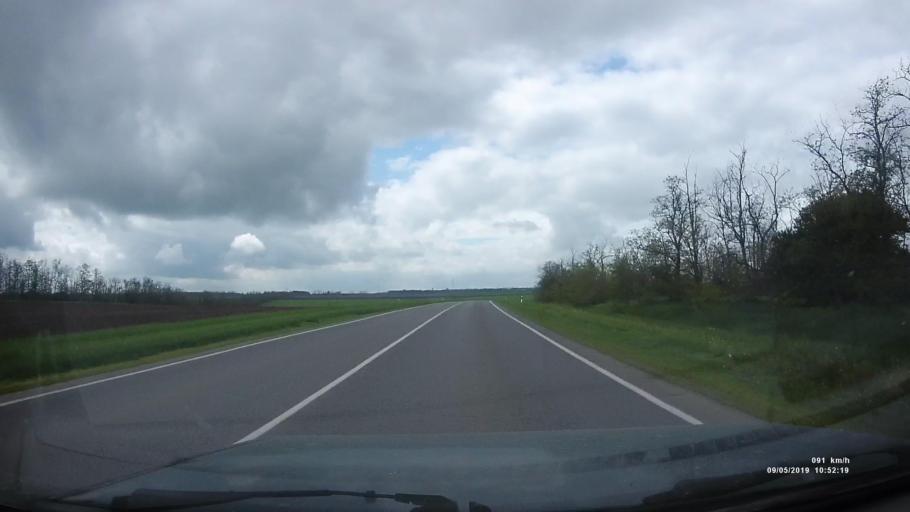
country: RU
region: Rostov
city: Peshkovo
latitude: 46.9023
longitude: 39.3538
